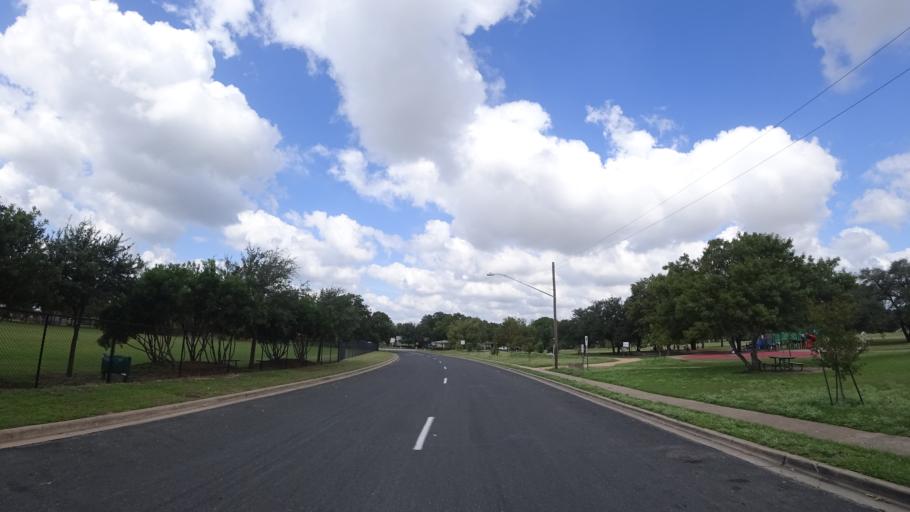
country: US
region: Texas
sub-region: Travis County
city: Austin
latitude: 30.3535
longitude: -97.7203
